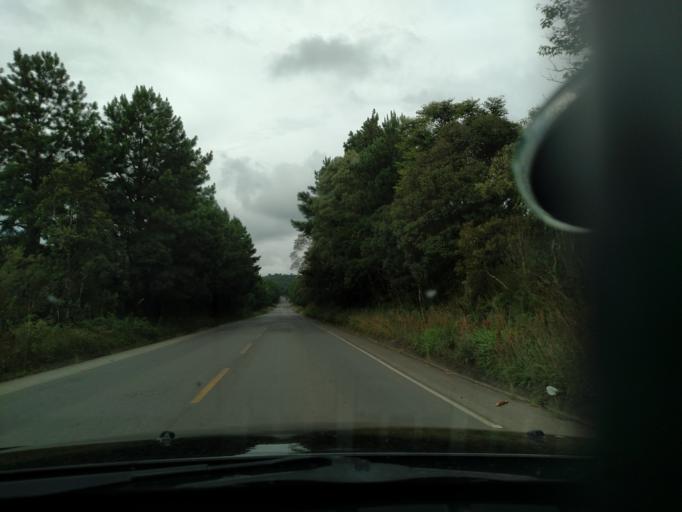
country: BR
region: Santa Catarina
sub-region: Otacilio Costa
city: Otacilio Costa
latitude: -27.6179
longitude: -50.1852
